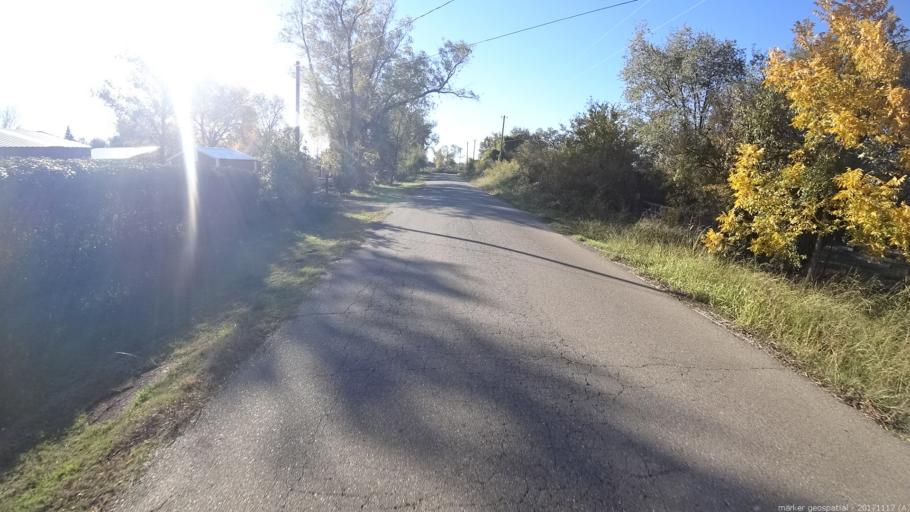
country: US
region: California
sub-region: Shasta County
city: Cottonwood
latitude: 40.4022
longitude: -122.2318
